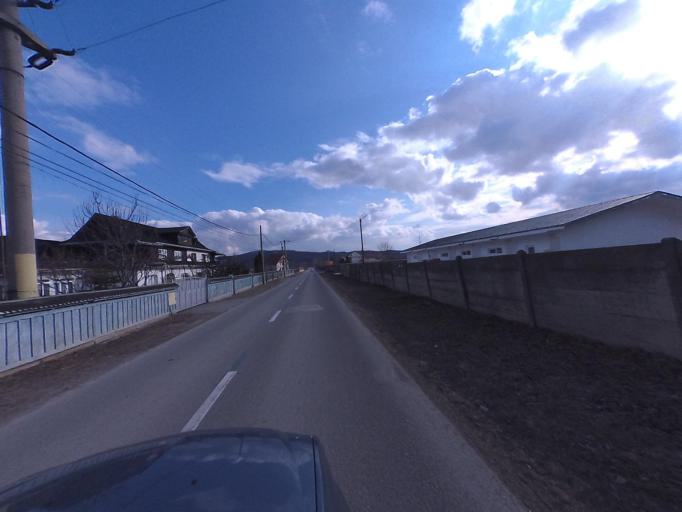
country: RO
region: Neamt
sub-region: Oras Targu Neamt
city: Targu Neamt
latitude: 47.2079
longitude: 26.3993
